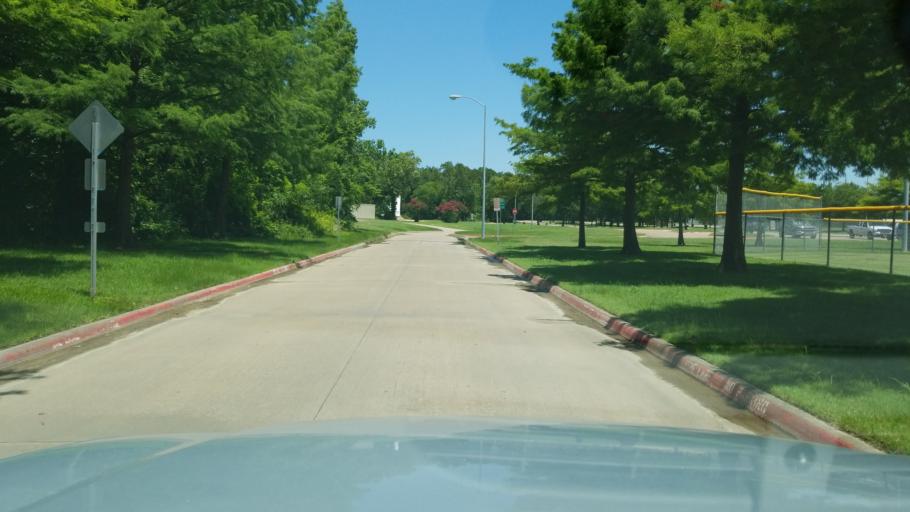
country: US
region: Texas
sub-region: Dallas County
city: Irving
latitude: 32.8106
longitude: -96.9137
